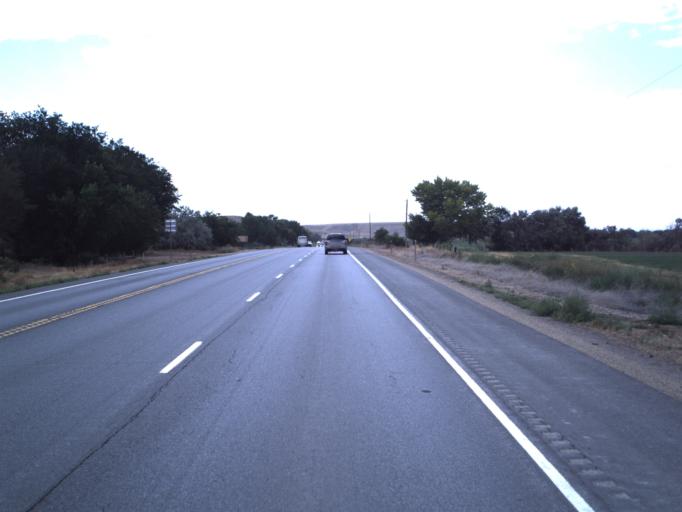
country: US
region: Utah
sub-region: Duchesne County
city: Duchesne
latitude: 40.1536
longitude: -110.2263
